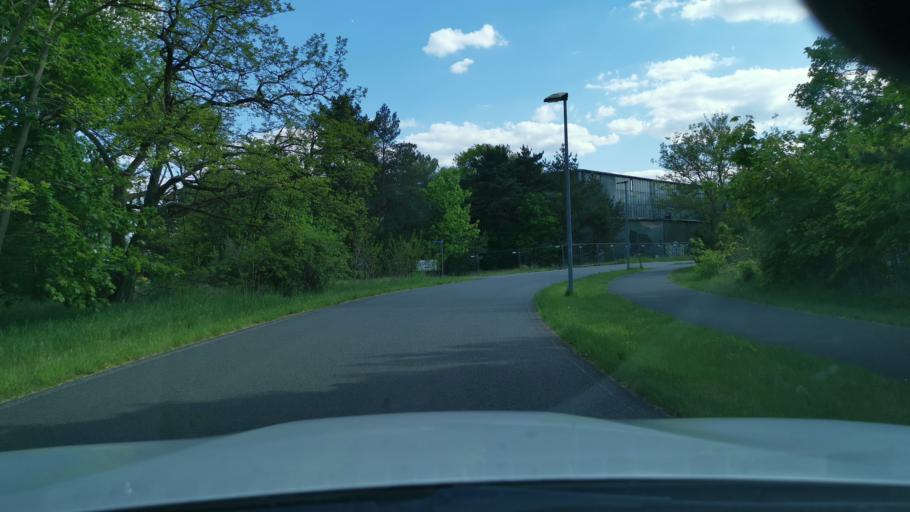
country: DE
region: Brandenburg
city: Niedergorsdorf
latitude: 52.0034
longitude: 12.9938
